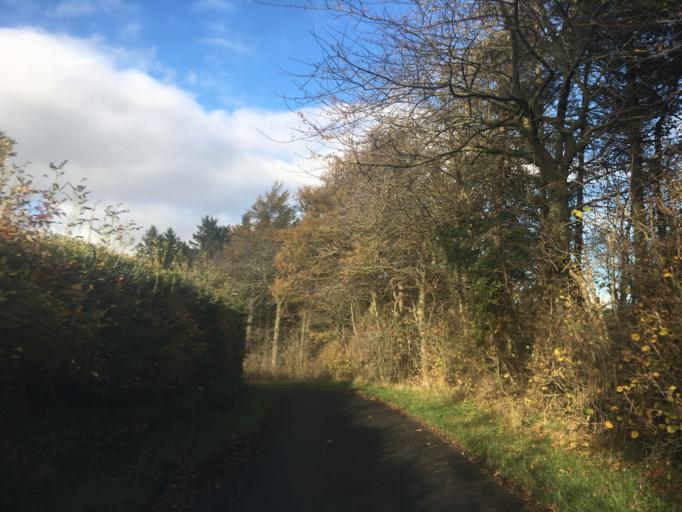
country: GB
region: Scotland
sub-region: East Lothian
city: Pencaitland
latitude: 55.8604
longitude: -2.8630
